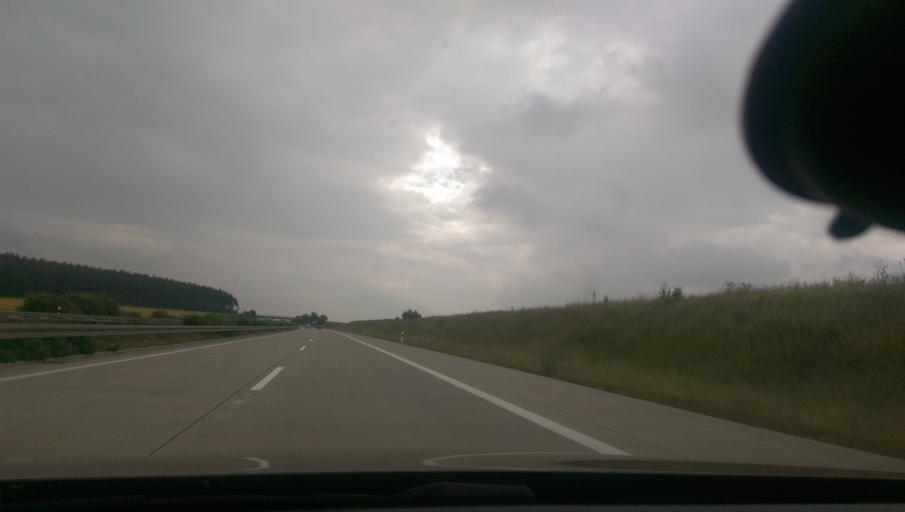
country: DE
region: Thuringia
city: Wingerode
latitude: 51.4015
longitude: 10.2330
